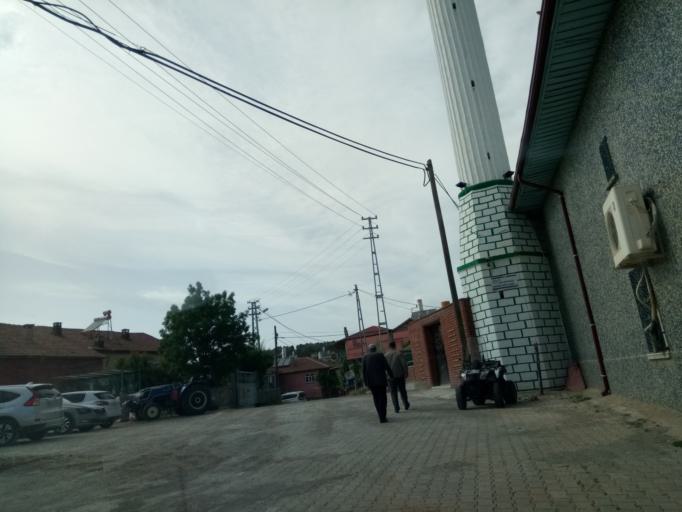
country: TR
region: Konya
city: Ahirli
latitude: 37.2870
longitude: 32.1795
